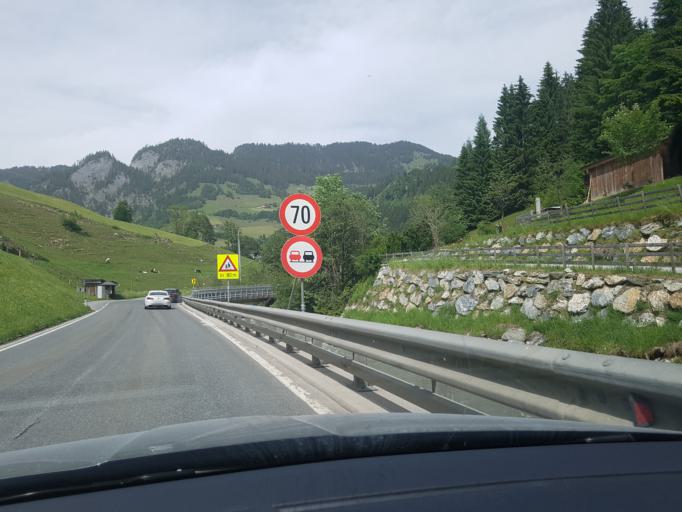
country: AT
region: Salzburg
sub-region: Politischer Bezirk Sankt Johann im Pongau
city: Sankt Johann im Pongau
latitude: 47.2774
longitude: 13.2145
